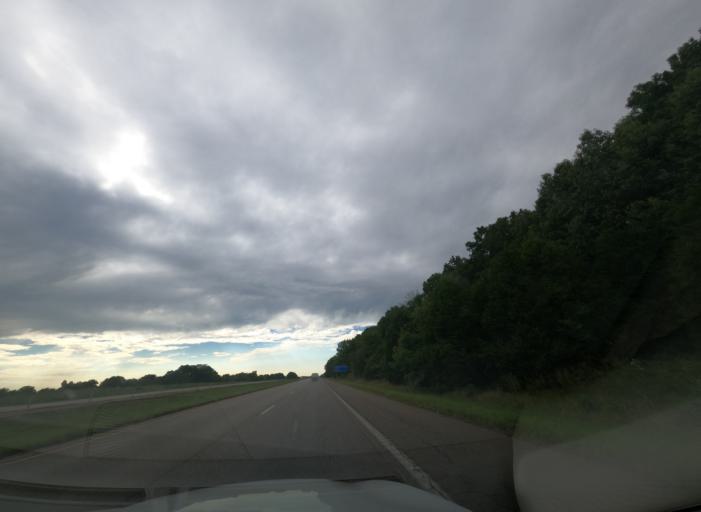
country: US
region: Missouri
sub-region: Sainte Genevieve County
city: Sainte Genevieve
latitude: 37.9257
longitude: -90.1008
